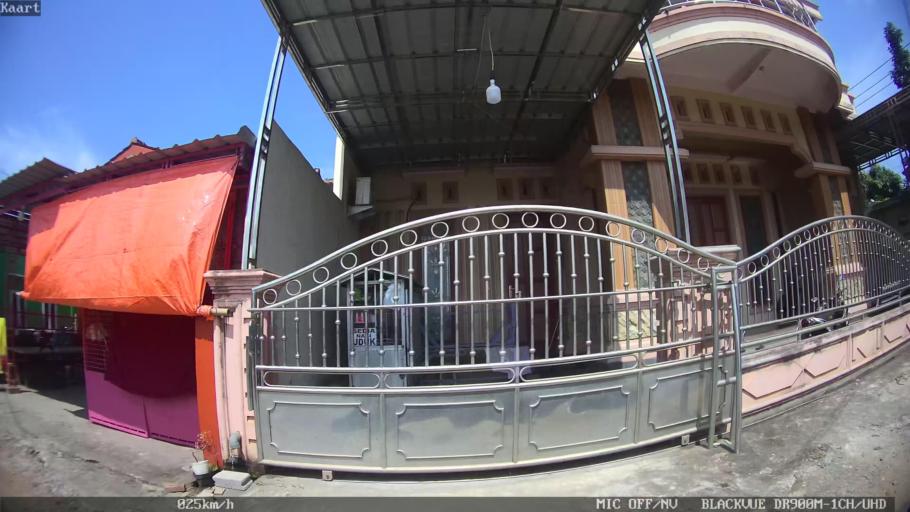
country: ID
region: Lampung
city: Kedaton
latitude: -5.3633
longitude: 105.2501
